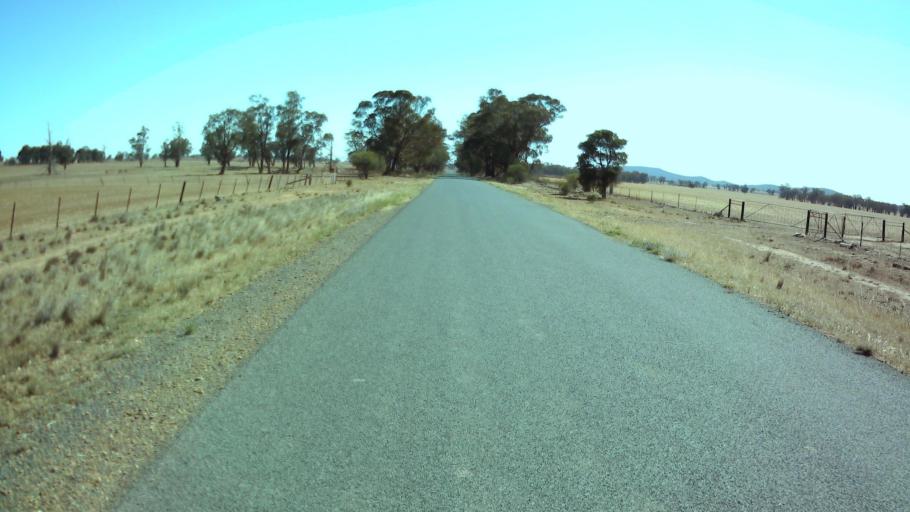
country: AU
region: New South Wales
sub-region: Weddin
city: Grenfell
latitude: -33.7436
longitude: 147.8793
